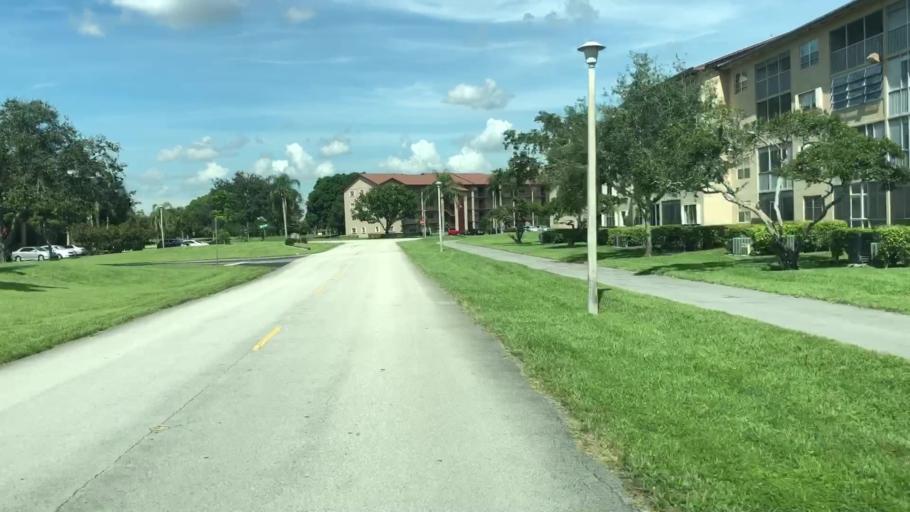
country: US
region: Florida
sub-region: Broward County
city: Sunshine Ranches
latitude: 26.0035
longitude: -80.3193
